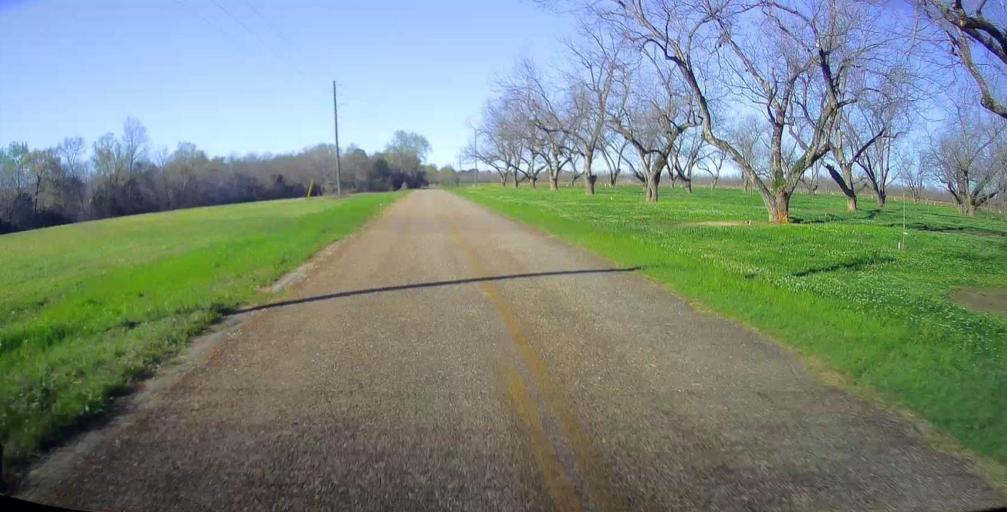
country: US
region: Georgia
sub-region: Macon County
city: Marshallville
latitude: 32.4857
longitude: -83.9521
